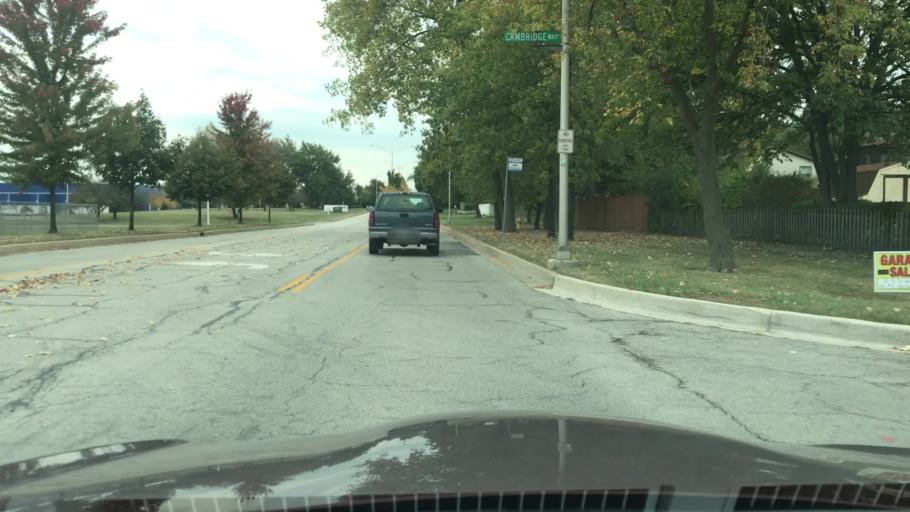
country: US
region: Illinois
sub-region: DuPage County
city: Woodridge
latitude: 41.7313
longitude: -88.0402
